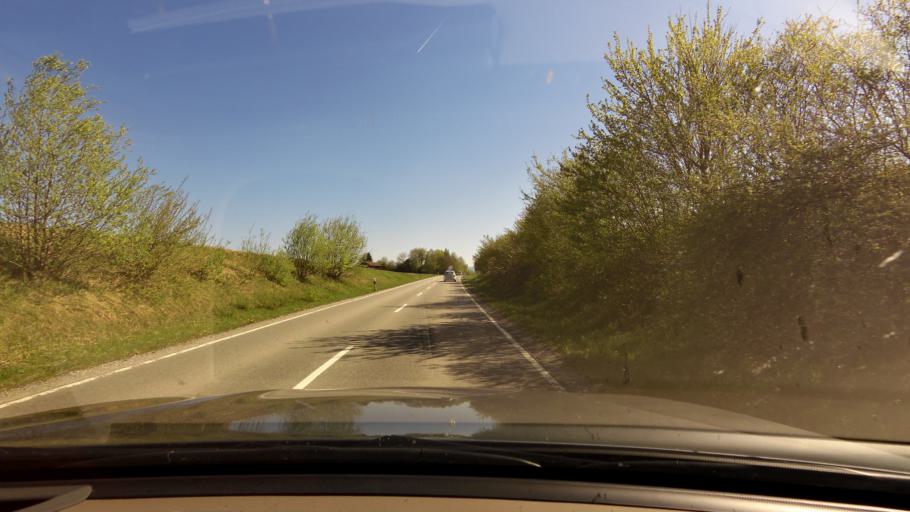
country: DE
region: Bavaria
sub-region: Upper Bavaria
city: Griesstatt
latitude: 47.9865
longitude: 12.1757
